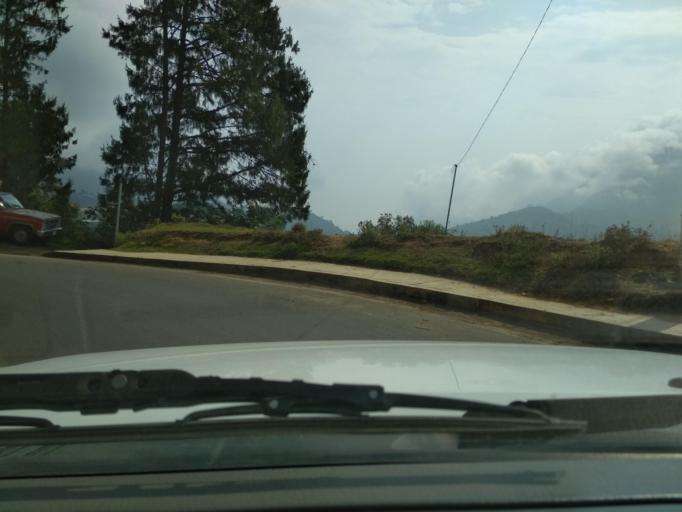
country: MX
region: Veracruz
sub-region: Soledad Atzompa
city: Tlatilpa
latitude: 18.7526
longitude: -97.1533
